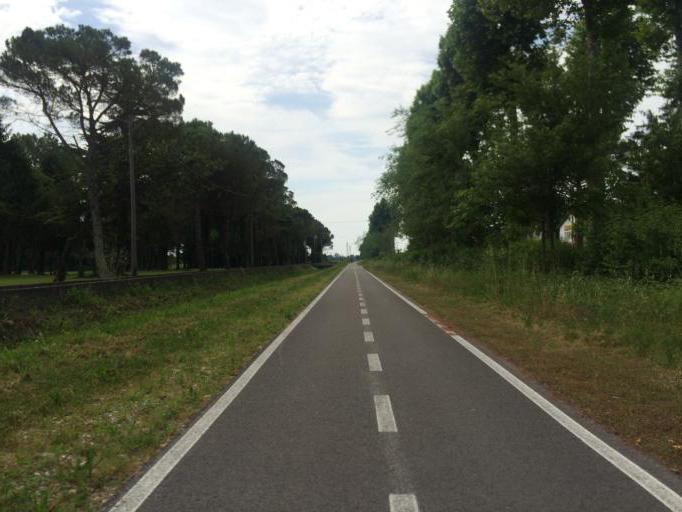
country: IT
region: Friuli Venezia Giulia
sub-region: Provincia di Udine
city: Aquileia
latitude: 45.7451
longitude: 13.3820
